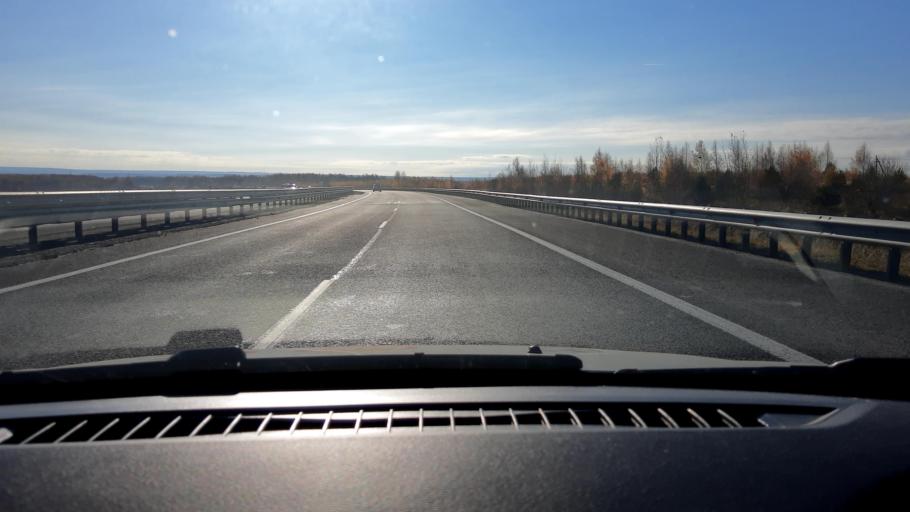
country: RU
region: Nizjnij Novgorod
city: Burevestnik
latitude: 56.1494
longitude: 43.7497
